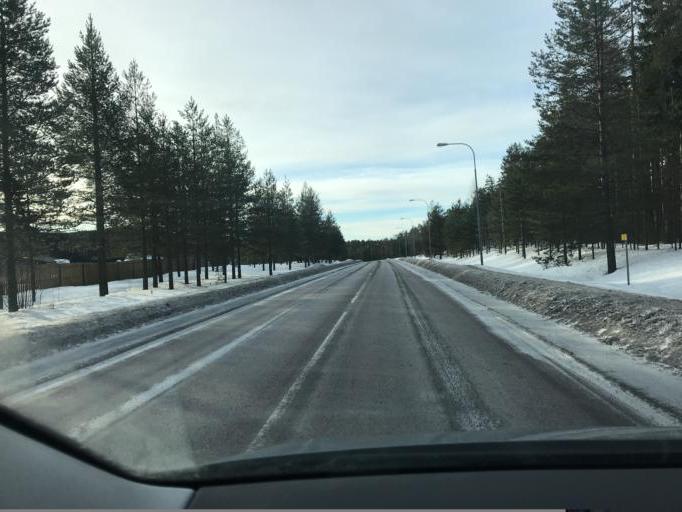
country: SE
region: Norrbotten
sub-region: Lulea Kommun
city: Gammelstad
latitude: 65.6244
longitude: 22.0358
